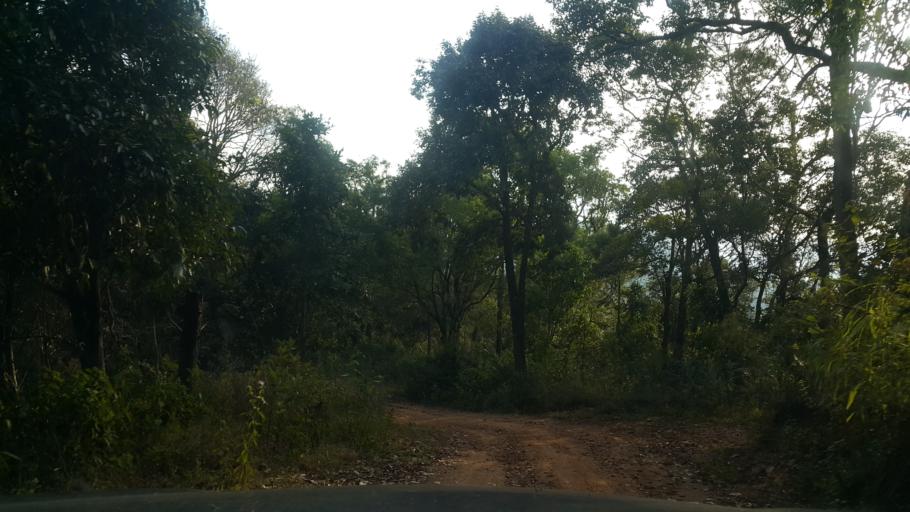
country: TH
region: Chiang Mai
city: Samoeng
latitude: 19.0295
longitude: 98.6471
